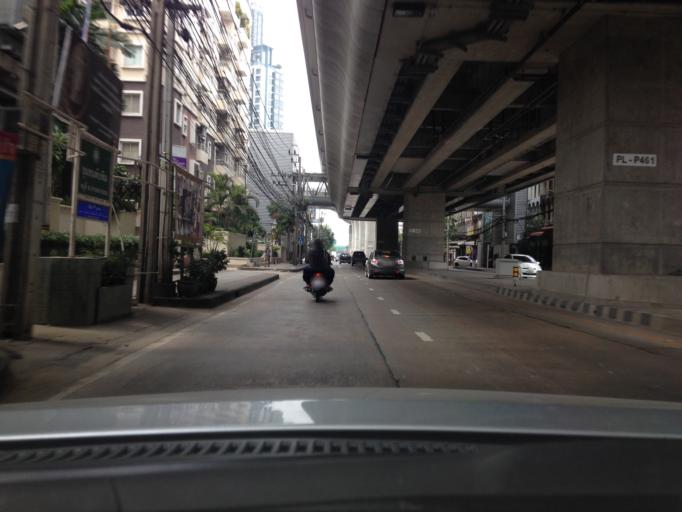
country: TH
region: Nonthaburi
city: Mueang Nonthaburi
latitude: 13.8398
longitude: 100.5146
